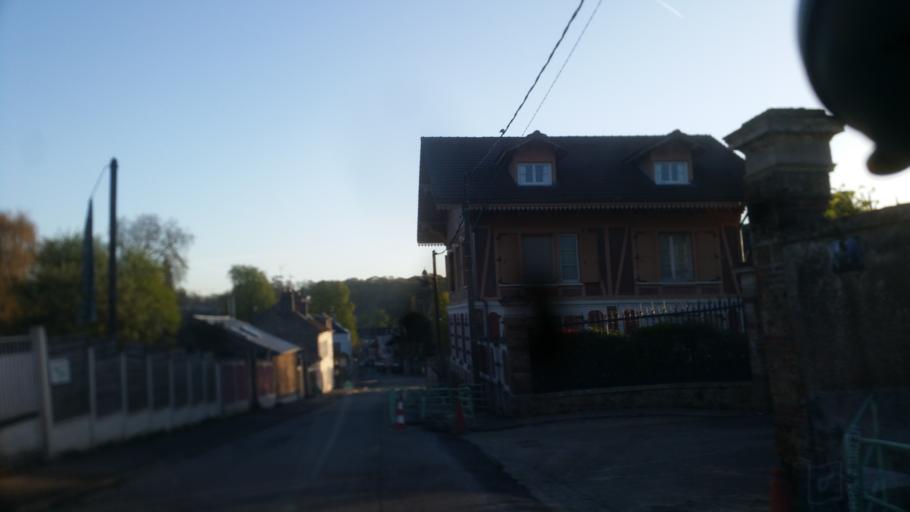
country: FR
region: Ile-de-France
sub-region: Departement de l'Essonne
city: Limours
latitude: 48.6432
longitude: 2.0750
